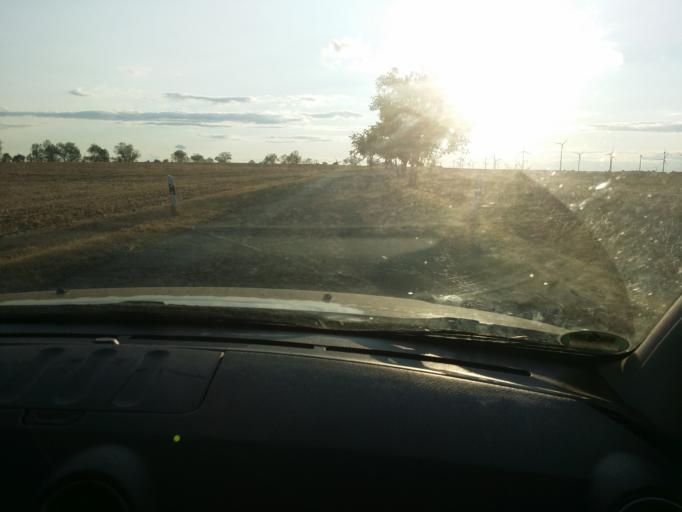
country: DE
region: Saxony-Anhalt
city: Labejum
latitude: 51.6142
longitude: 11.9111
